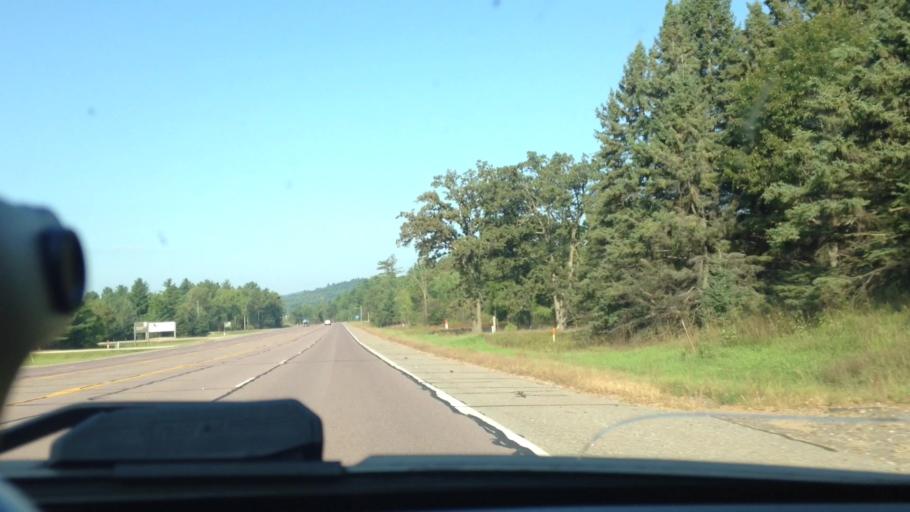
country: US
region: Michigan
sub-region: Dickinson County
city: Quinnesec
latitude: 45.8028
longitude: -87.9620
